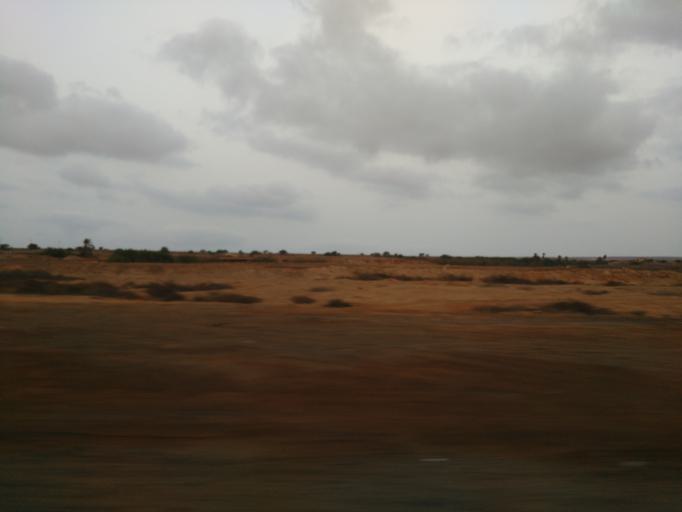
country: CV
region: Sal
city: Espargos
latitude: 16.6785
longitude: -22.9335
